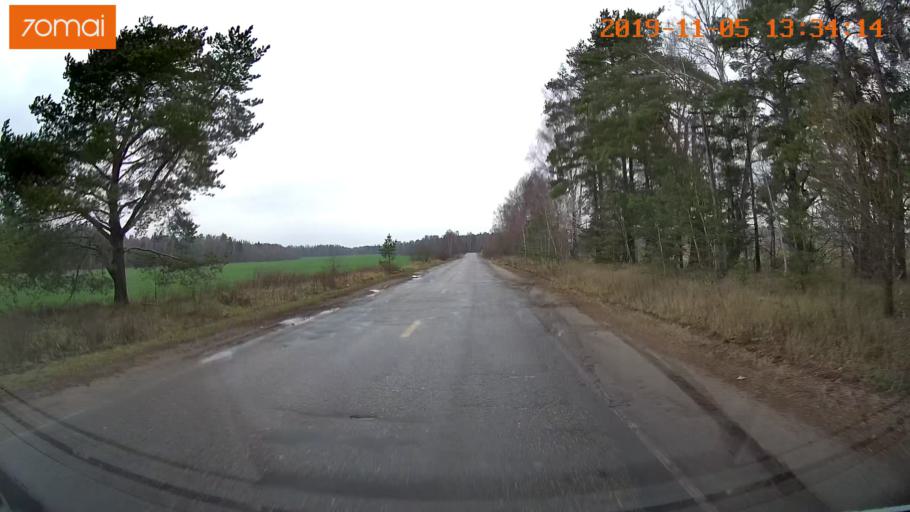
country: RU
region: Ivanovo
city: Shuya
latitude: 56.8989
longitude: 41.3901
